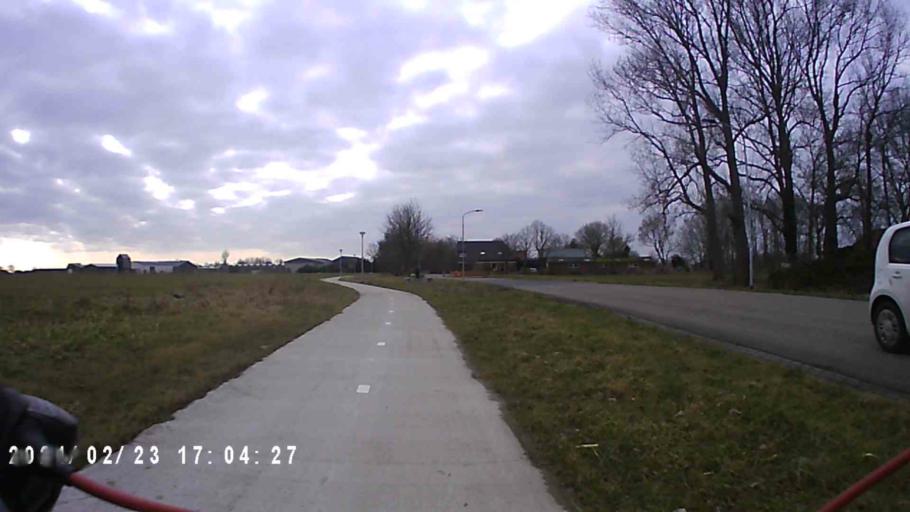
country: NL
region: Groningen
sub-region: Gemeente De Marne
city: Ulrum
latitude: 53.3879
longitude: 6.3824
